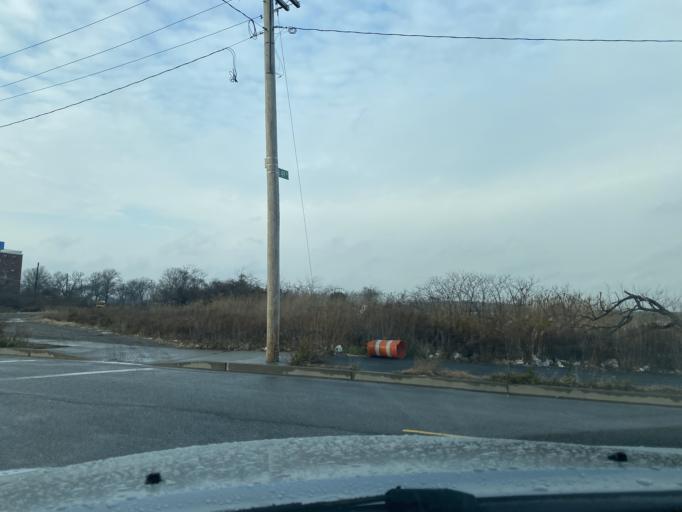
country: US
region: New York
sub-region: Nassau County
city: Inwood
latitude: 40.5962
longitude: -73.7803
